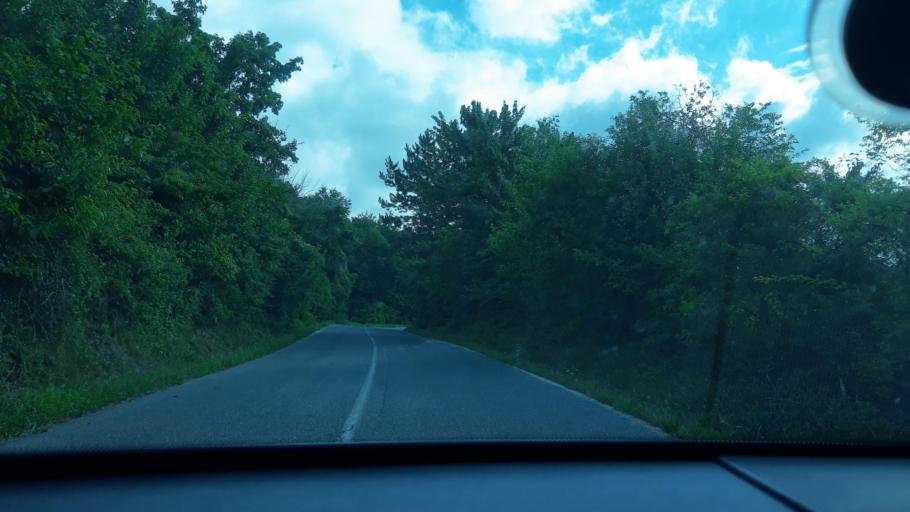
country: SK
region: Trnavsky
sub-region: Okres Trnava
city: Piestany
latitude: 48.6549
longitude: 17.9517
